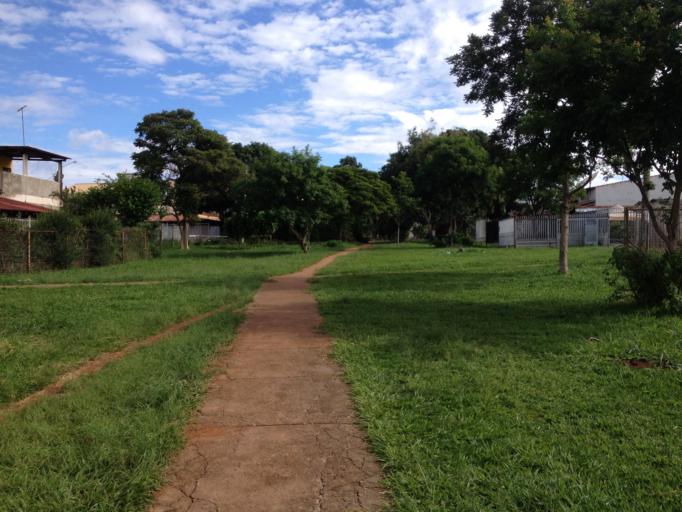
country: BR
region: Federal District
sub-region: Brasilia
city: Brasilia
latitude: -15.8451
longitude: -47.9793
